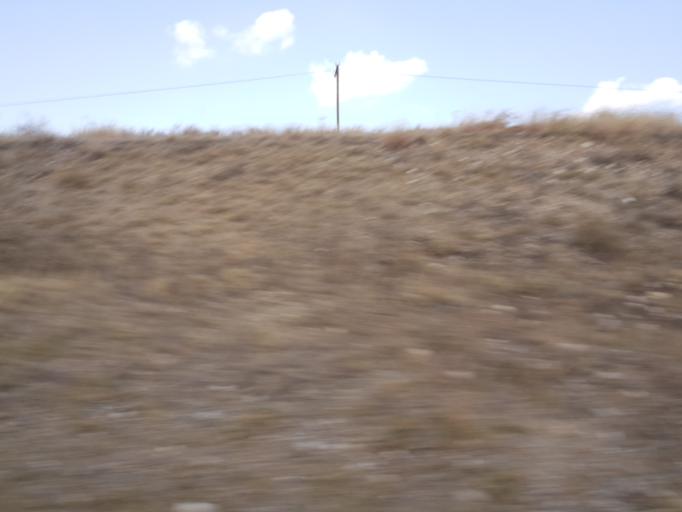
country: TR
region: Corum
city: Bogazkale
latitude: 40.1327
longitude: 34.5514
